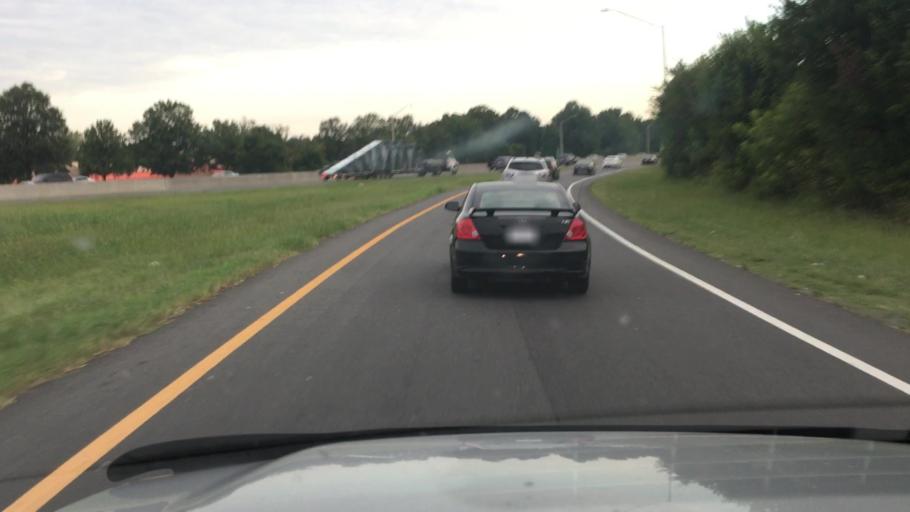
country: US
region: North Carolina
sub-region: Mecklenburg County
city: Pineville
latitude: 35.0921
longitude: -80.8745
